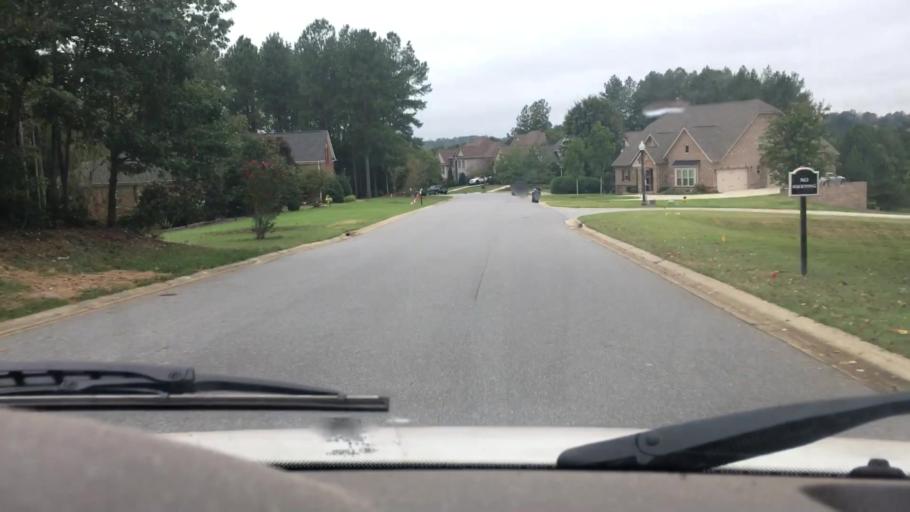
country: US
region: North Carolina
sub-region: Lincoln County
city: Denver
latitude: 35.4845
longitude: -81.0238
